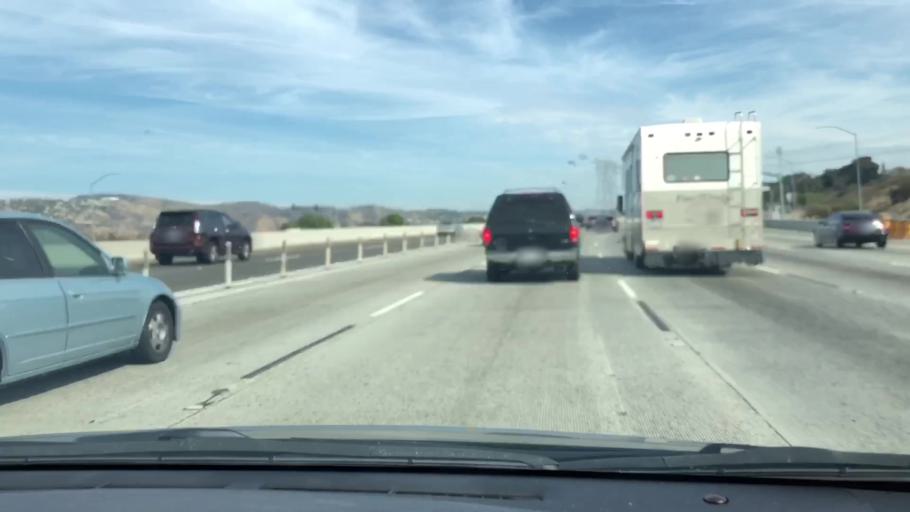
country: US
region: California
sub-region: Orange County
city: Yorba Linda
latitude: 33.8683
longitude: -117.7597
